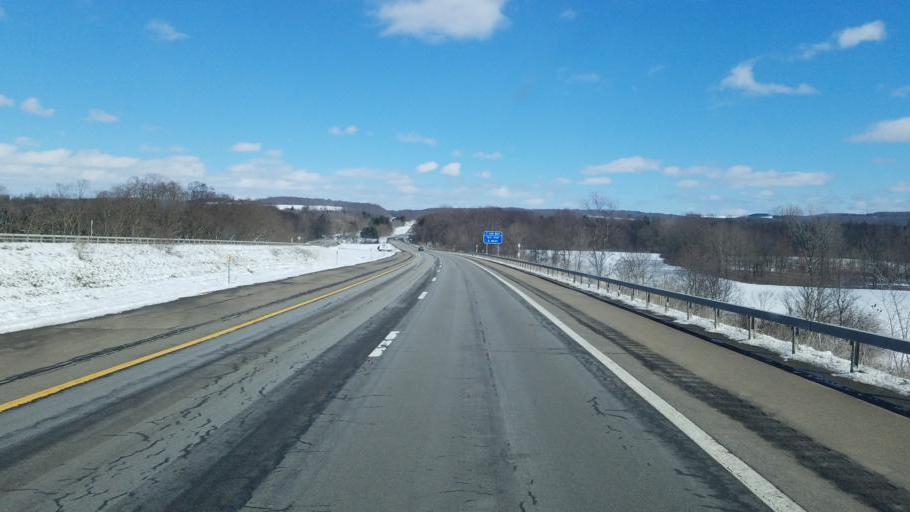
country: US
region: New York
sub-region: Chautauqua County
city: Falconer
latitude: 42.1398
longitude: -79.1089
